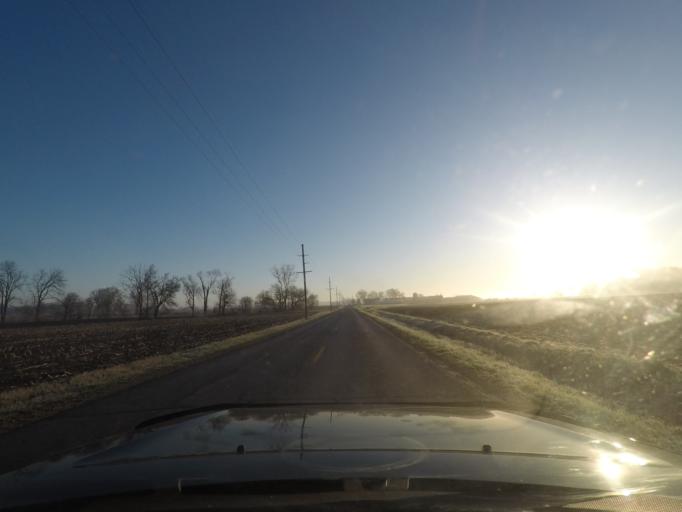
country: US
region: Indiana
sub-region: Elkhart County
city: Wakarusa
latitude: 41.4881
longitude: -86.0337
